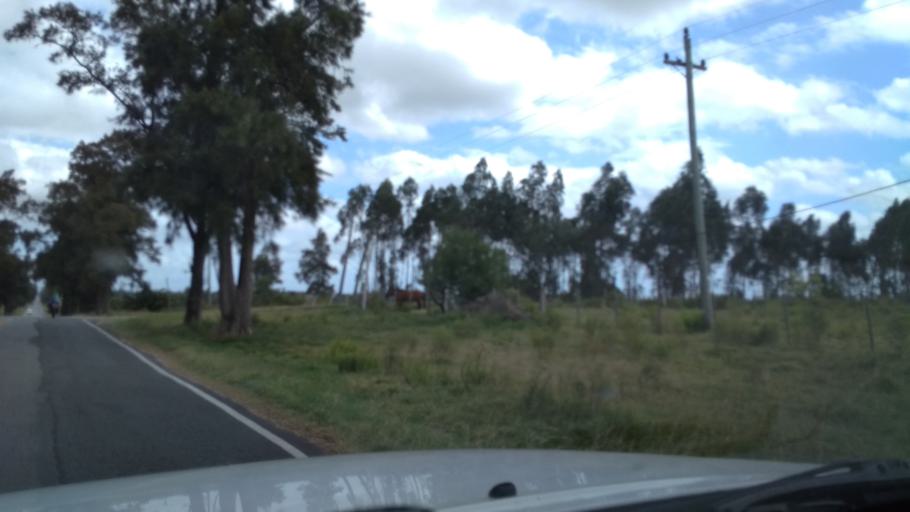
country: UY
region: Canelones
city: San Bautista
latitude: -34.4034
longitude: -55.9598
